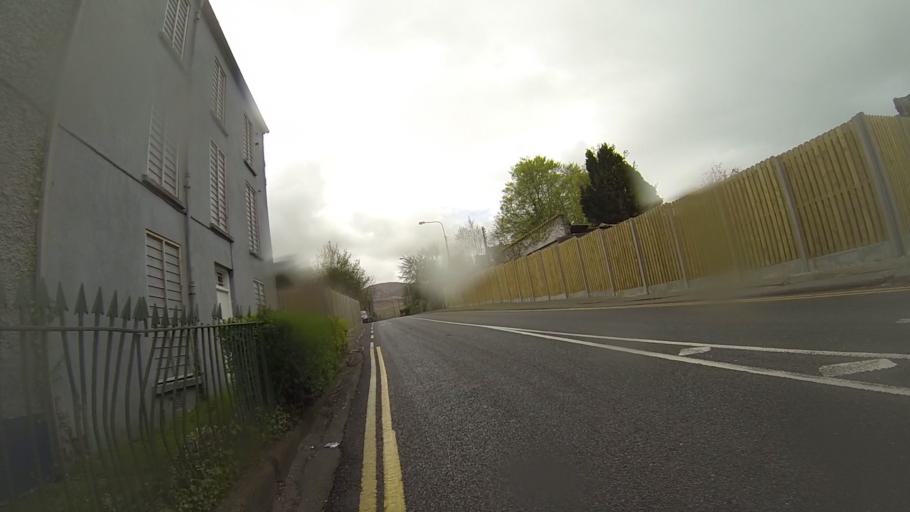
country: IE
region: Munster
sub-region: Ciarrai
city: Kenmare
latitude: 51.8779
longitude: -9.5834
